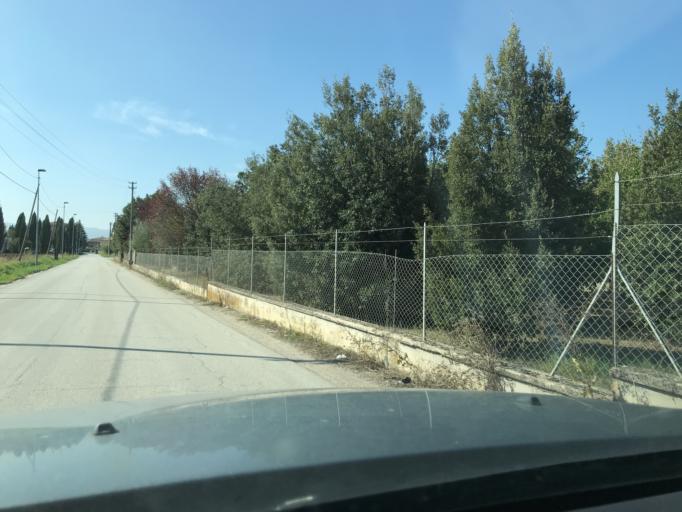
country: IT
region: Umbria
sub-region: Provincia di Perugia
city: Ospedalicchio
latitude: 43.0823
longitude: 12.5059
